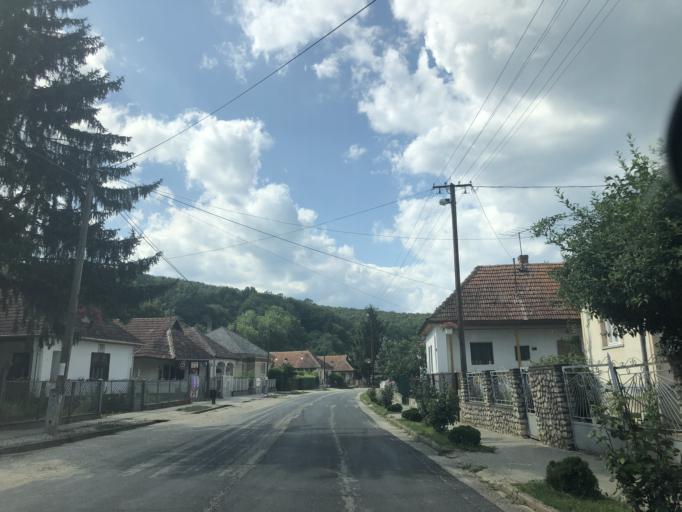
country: HU
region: Borsod-Abauj-Zemplen
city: Szendro
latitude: 48.4396
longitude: 20.7950
